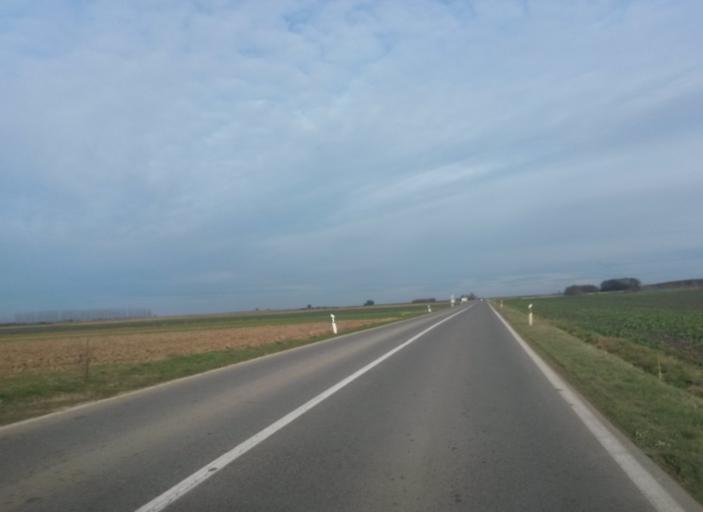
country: HR
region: Osjecko-Baranjska
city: Viskovci
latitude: 45.3612
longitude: 18.4267
